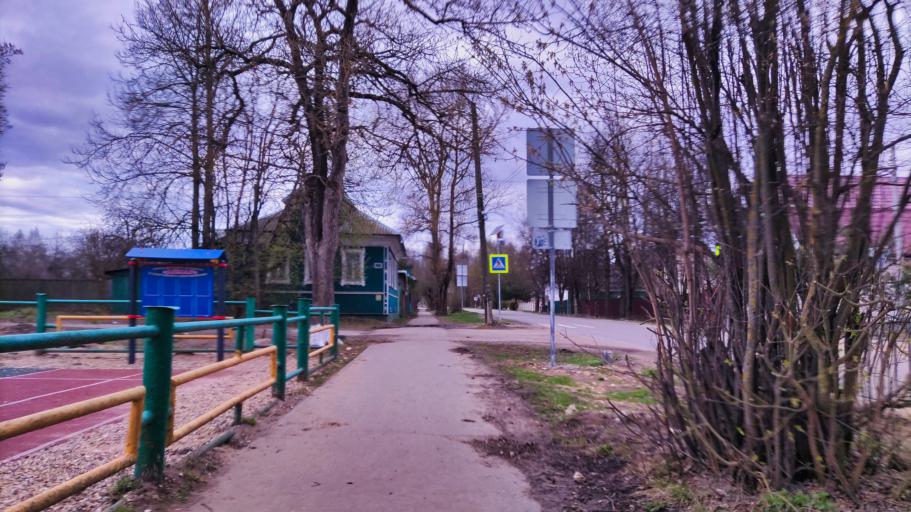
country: RU
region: Tverskaya
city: Rzhev
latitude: 56.2509
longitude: 34.3354
